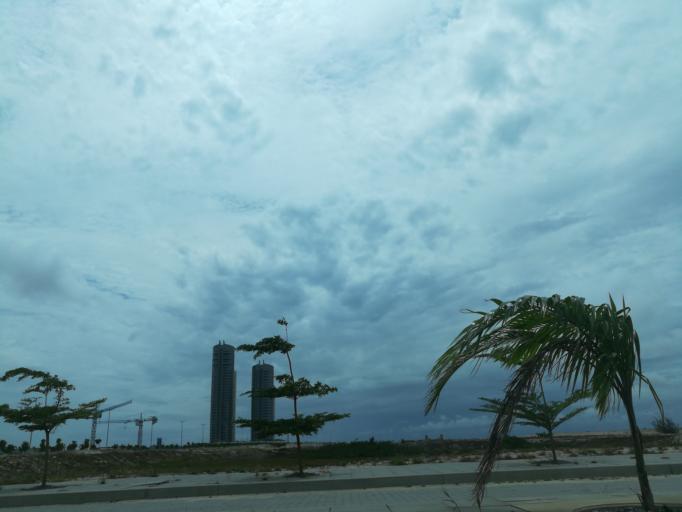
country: NG
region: Lagos
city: Lagos
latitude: 6.4108
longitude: 3.4042
